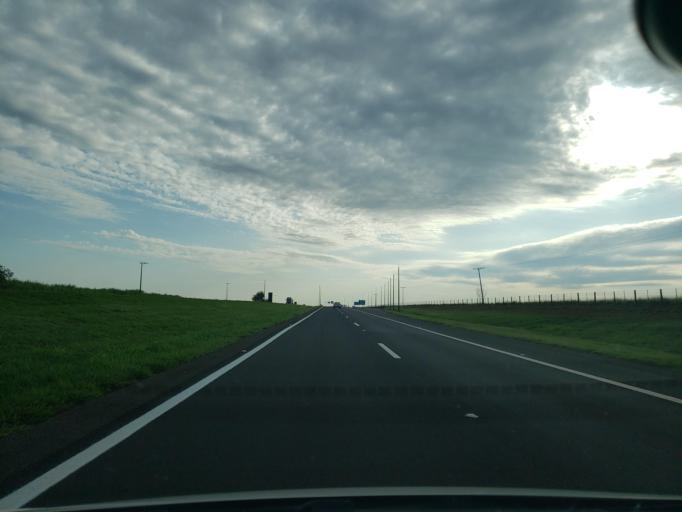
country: BR
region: Sao Paulo
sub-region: Guararapes
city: Guararapes
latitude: -21.2127
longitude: -50.7136
